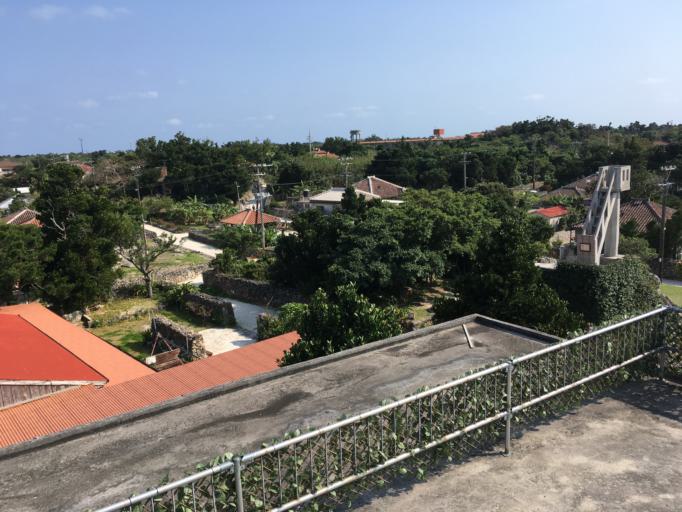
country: JP
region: Okinawa
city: Ishigaki
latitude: 24.3311
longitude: 124.0855
